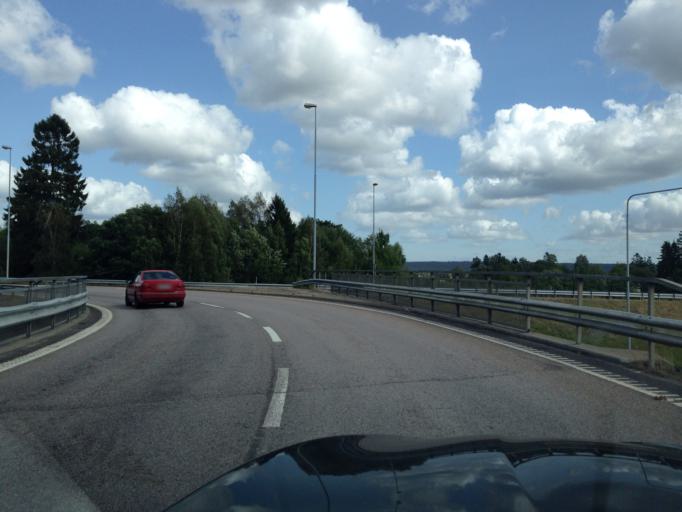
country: SE
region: Vaestra Goetaland
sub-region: Trollhattan
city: Trollhattan
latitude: 58.2991
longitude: 12.3329
